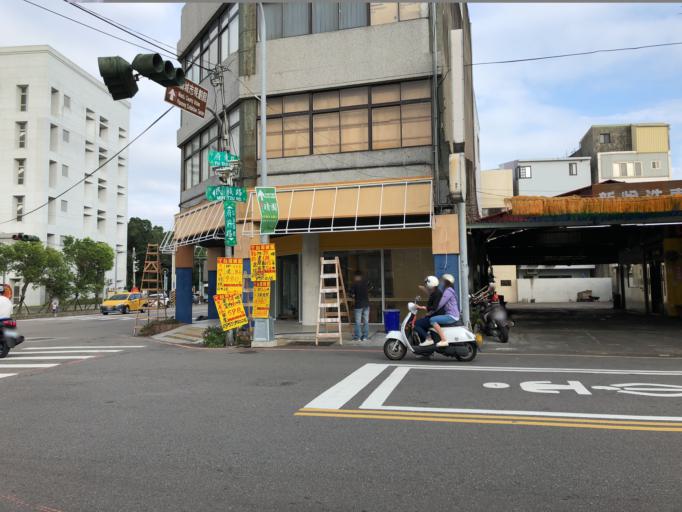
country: TW
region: Taiwan
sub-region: Miaoli
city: Miaoli
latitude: 24.5627
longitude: 120.8201
